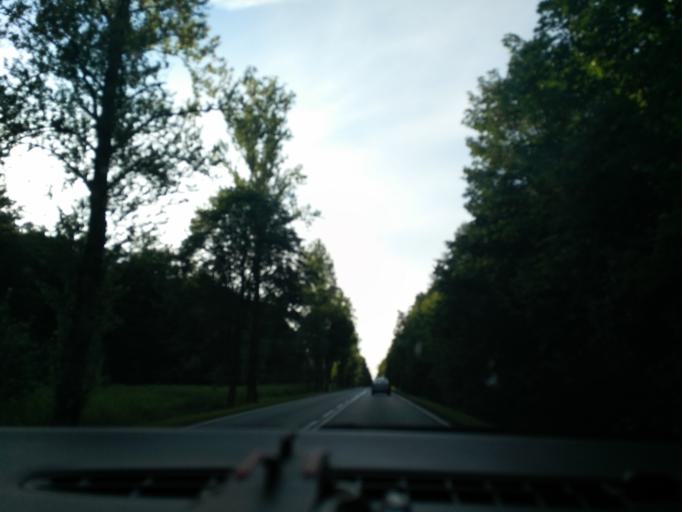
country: PL
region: Lublin Voivodeship
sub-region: Powiat krasnicki
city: Szastarka
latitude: 50.8472
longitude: 22.2920
